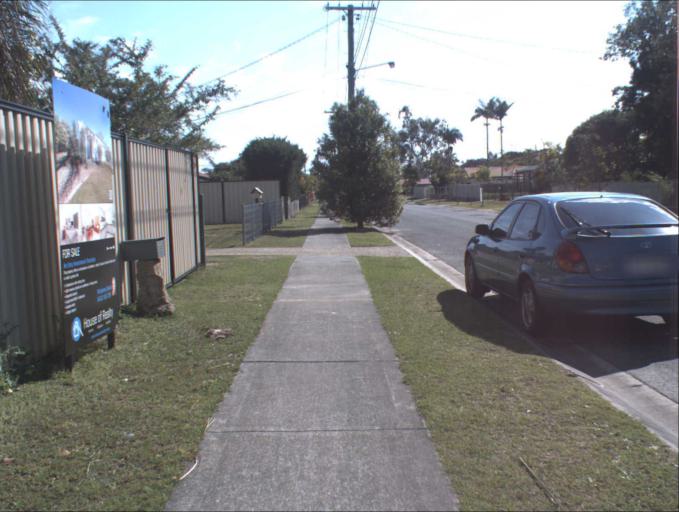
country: AU
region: Queensland
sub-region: Logan
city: Logan Reserve
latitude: -27.6833
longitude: 153.0895
